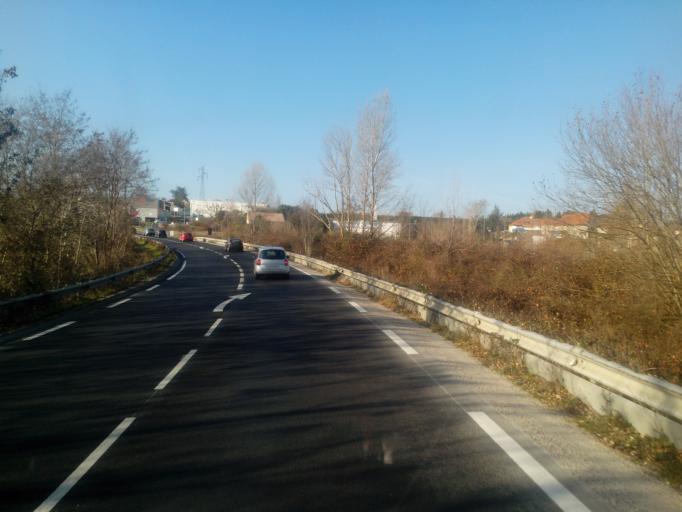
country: FR
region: Midi-Pyrenees
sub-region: Departement de l'Aveyron
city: Capdenac-Gare
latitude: 44.5931
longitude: 2.0642
